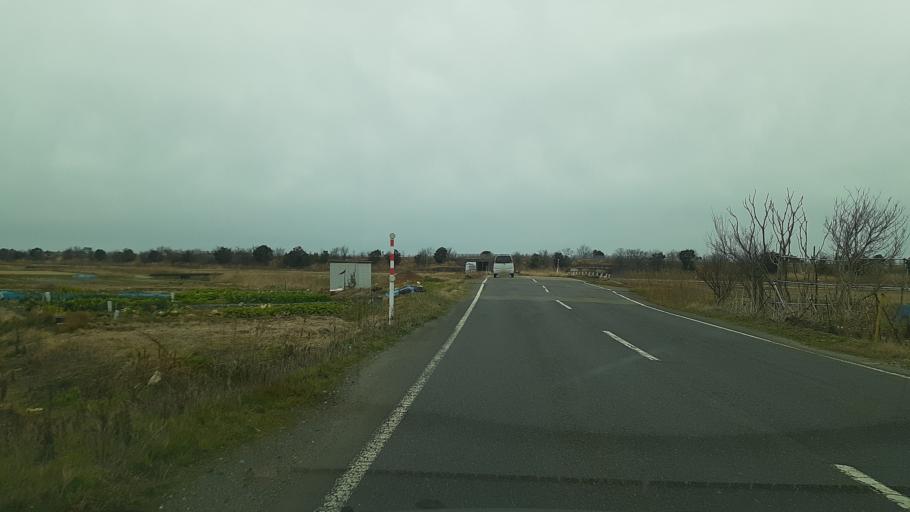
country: JP
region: Niigata
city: Niitsu-honcho
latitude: 37.8197
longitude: 139.0844
